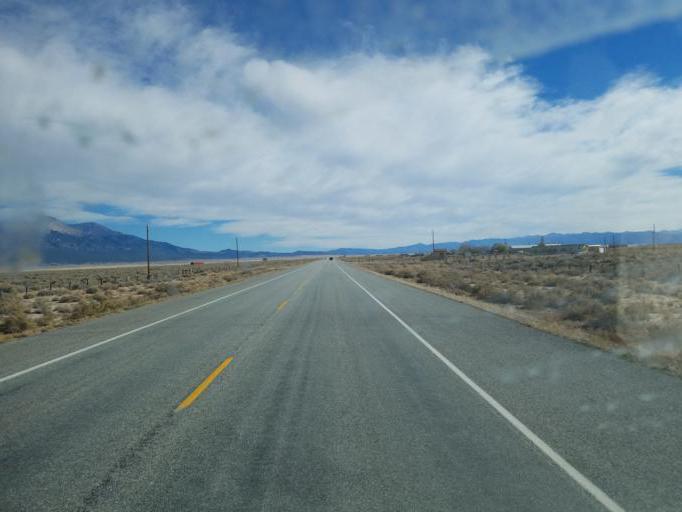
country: US
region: Colorado
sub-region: Alamosa County
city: Alamosa East
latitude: 37.4745
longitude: -105.7132
